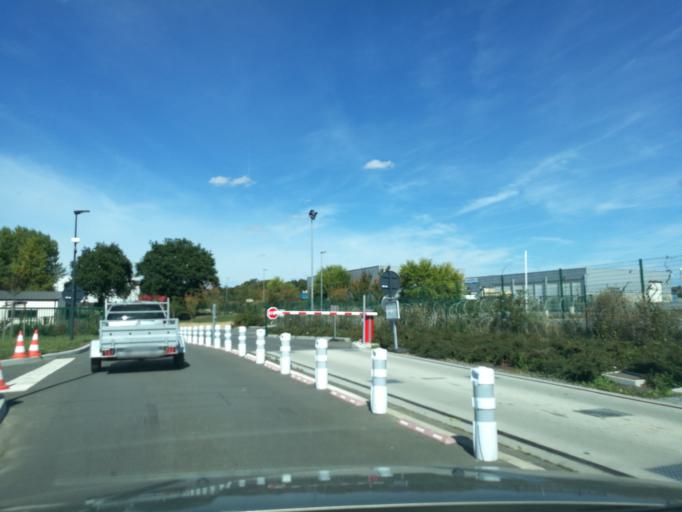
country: FR
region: Brittany
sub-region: Departement d'Ille-et-Vilaine
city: Montfort-sur-Meu
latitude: 48.1356
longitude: -1.9336
